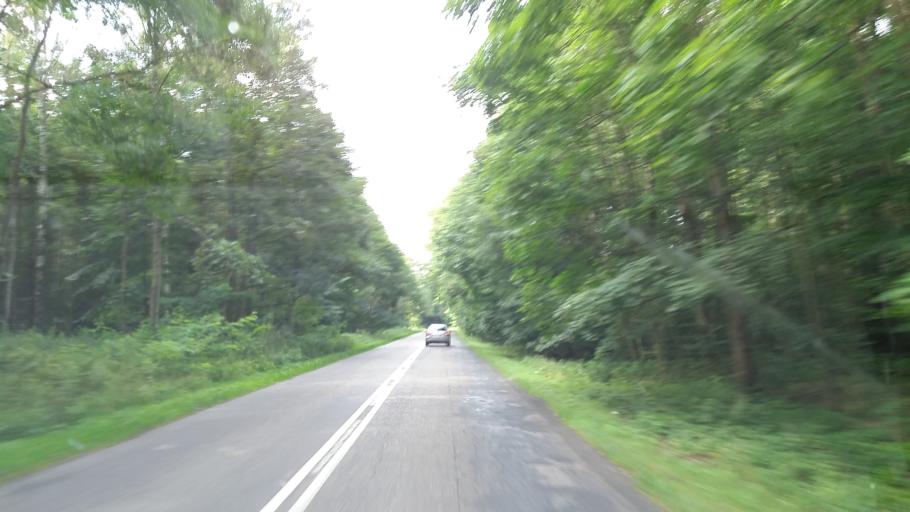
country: PL
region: West Pomeranian Voivodeship
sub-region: Powiat choszczenski
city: Pelczyce
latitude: 53.0785
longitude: 15.2870
